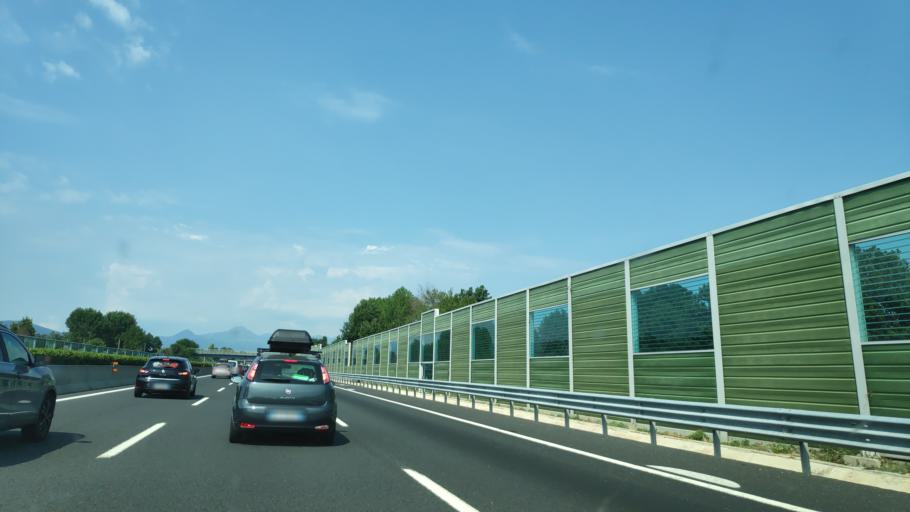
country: IT
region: Latium
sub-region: Provincia di Frosinone
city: Pofi
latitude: 41.5541
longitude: 13.4350
